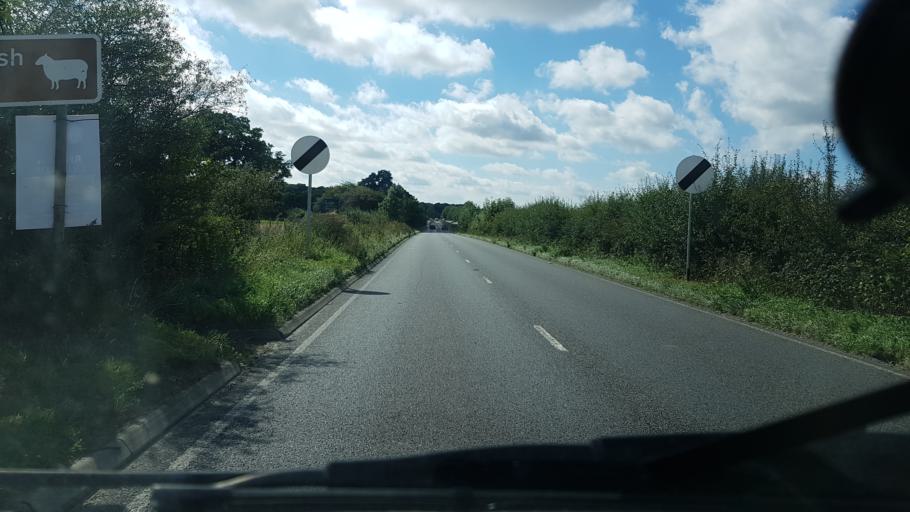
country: GB
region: England
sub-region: West Sussex
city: Bewbush
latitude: 51.0963
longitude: -0.2459
